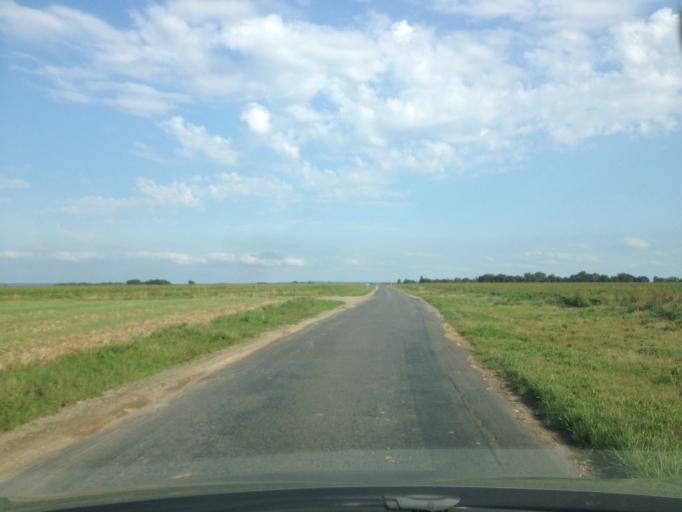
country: FR
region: Lower Normandy
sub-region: Departement du Calvados
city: Canon
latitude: 49.0675
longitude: -0.1174
